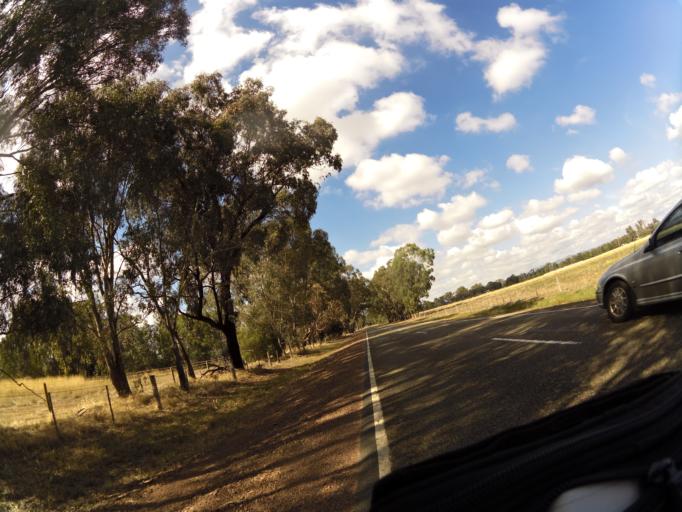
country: AU
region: Victoria
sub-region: Benalla
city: Benalla
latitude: -36.5881
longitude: 146.0090
